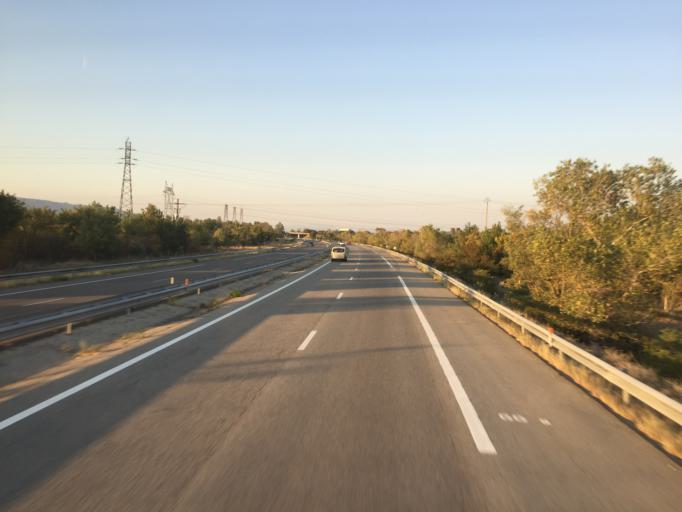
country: FR
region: Provence-Alpes-Cote d'Azur
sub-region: Departement des Alpes-de-Haute-Provence
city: Sainte-Tulle
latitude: 43.7750
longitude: 5.7991
